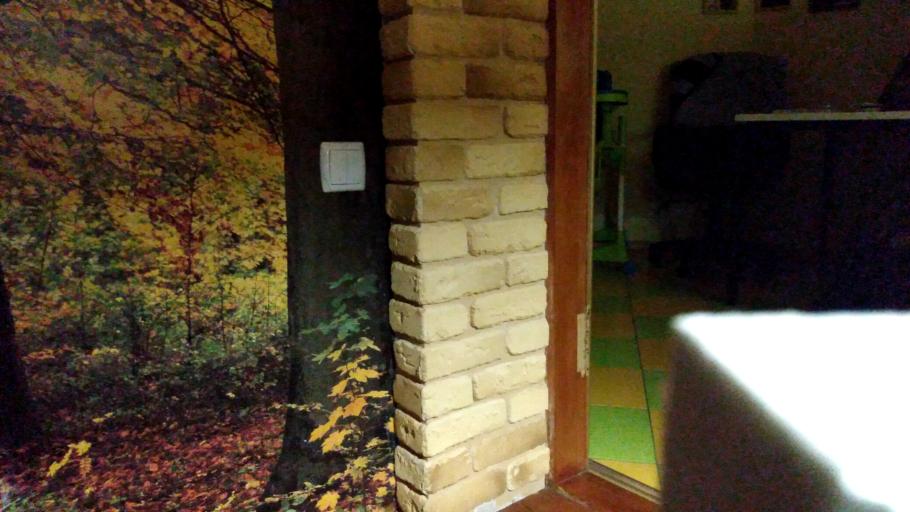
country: RU
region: Vologda
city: Lipin Bor
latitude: 60.9464
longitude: 37.9802
